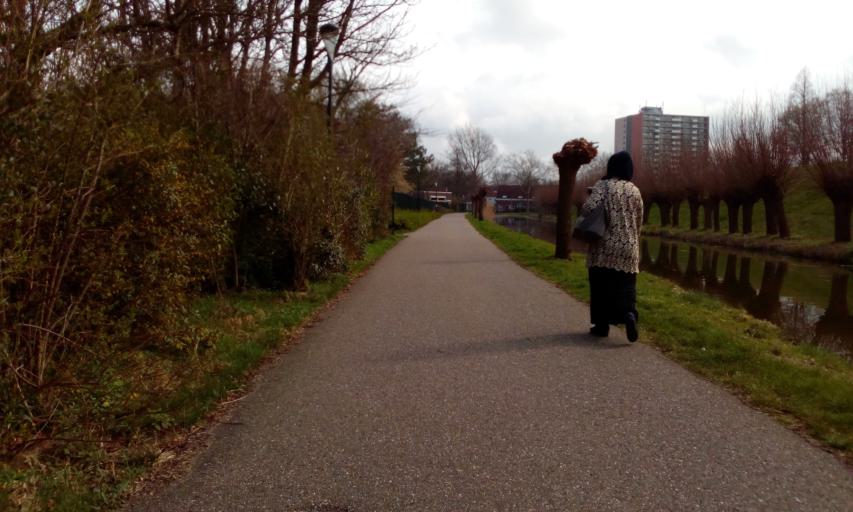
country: NL
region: South Holland
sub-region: Gemeente Maassluis
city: Maassluis
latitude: 51.9285
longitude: 4.2492
